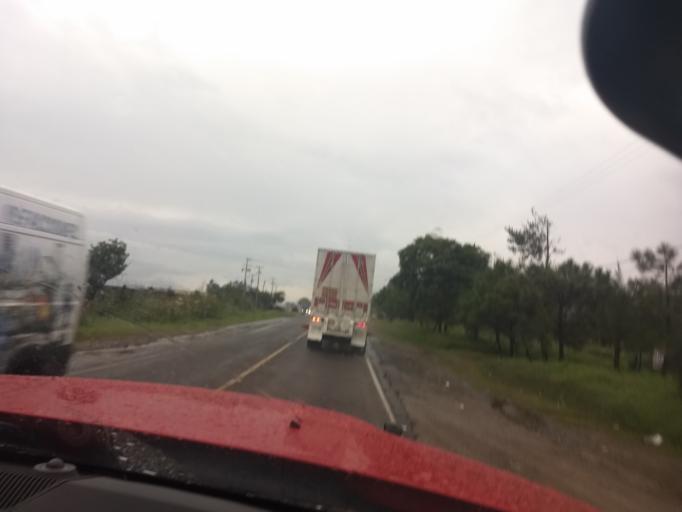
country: MX
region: Jalisco
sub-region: Zapotlan el Grande
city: Ciudad Guzman [CERESO]
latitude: 19.6499
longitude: -103.4731
